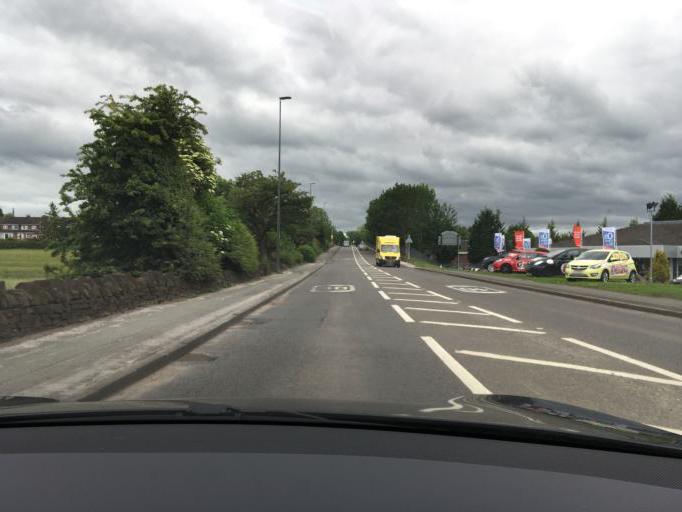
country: GB
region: England
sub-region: Cheshire East
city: Macclesfield
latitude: 53.2388
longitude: -2.1267
